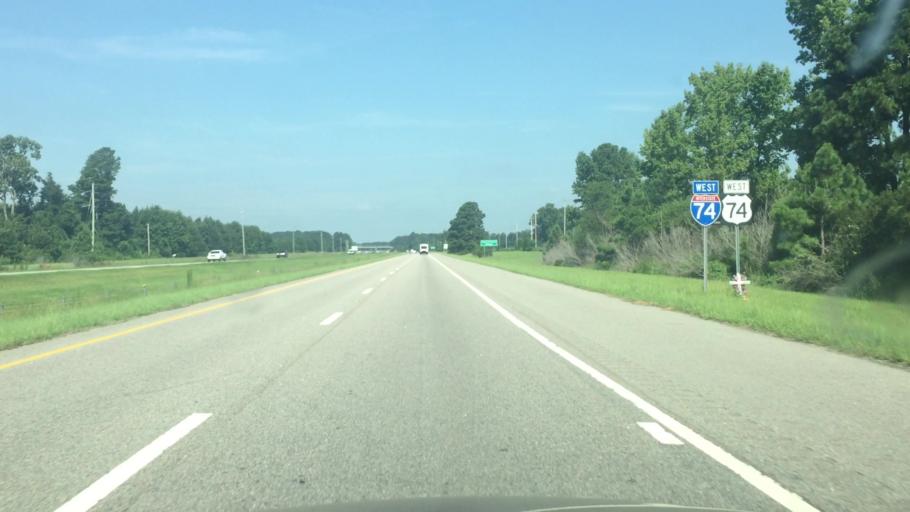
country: US
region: North Carolina
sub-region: Robeson County
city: Lumberton
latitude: 34.5834
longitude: -79.0548
